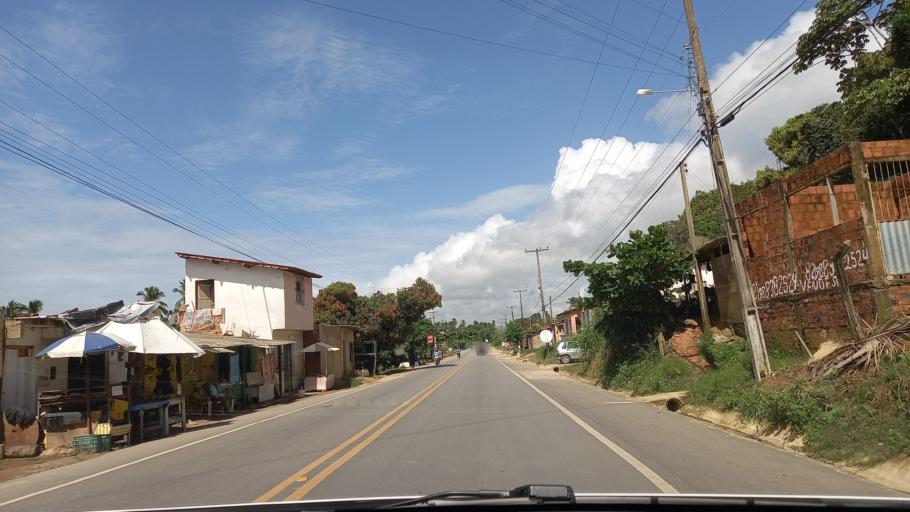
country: BR
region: Alagoas
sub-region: Maragogi
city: Maragogi
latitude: -8.9874
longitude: -35.1992
